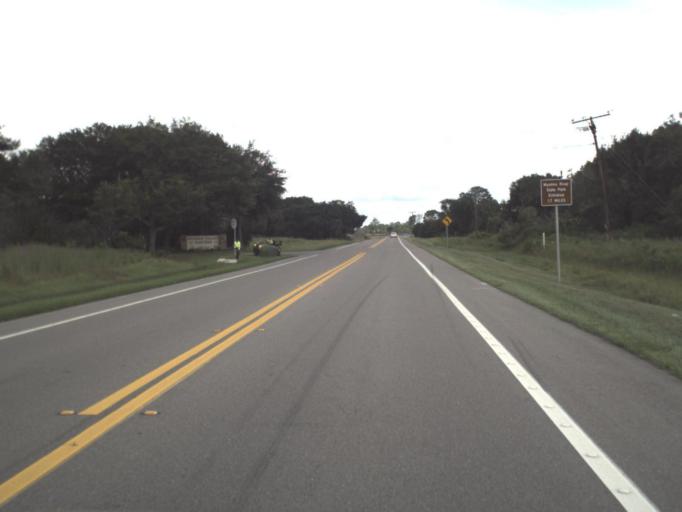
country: US
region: Florida
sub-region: Sarasota County
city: Lake Sarasota
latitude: 27.2436
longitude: -82.3445
